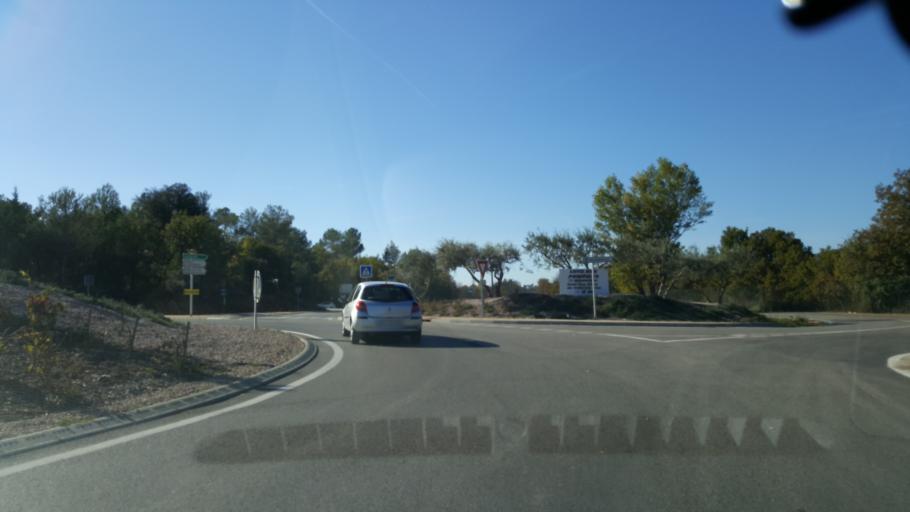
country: FR
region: Provence-Alpes-Cote d'Azur
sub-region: Departement du Var
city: Nans-les-Pins
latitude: 43.3931
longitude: 5.7978
